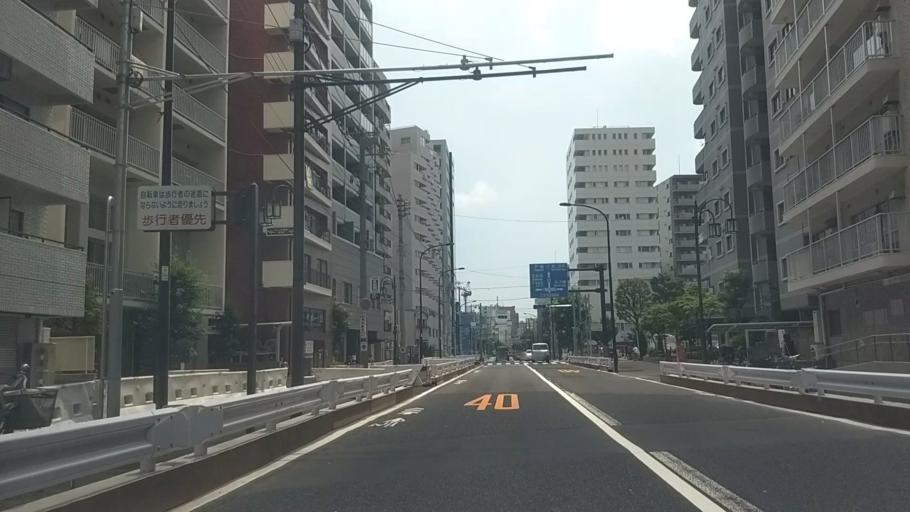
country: JP
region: Tokyo
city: Tokyo
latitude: 35.6166
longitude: 139.7072
